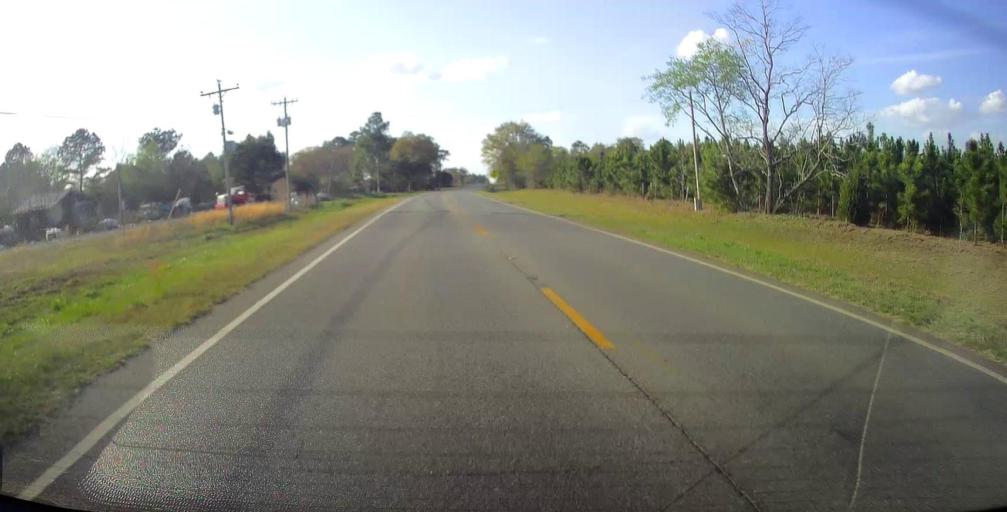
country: US
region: Georgia
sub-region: Toombs County
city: Lyons
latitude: 32.1857
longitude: -82.2995
